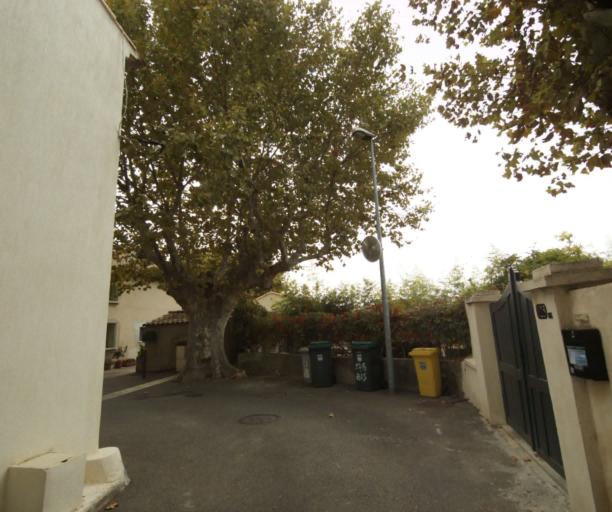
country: FR
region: Provence-Alpes-Cote d'Azur
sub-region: Departement des Bouches-du-Rhone
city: Saint-Victoret
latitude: 43.4181
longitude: 5.2528
